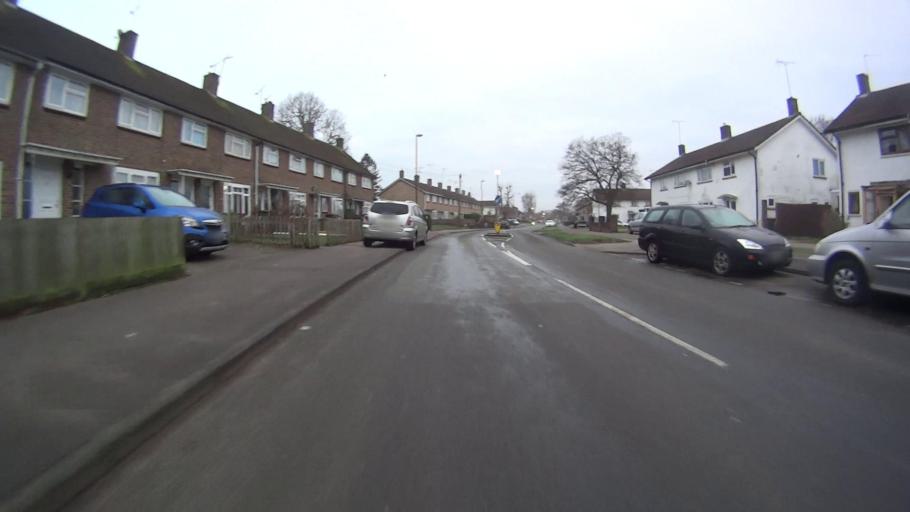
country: GB
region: England
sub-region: West Sussex
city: Crawley
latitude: 51.0998
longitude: -0.1844
